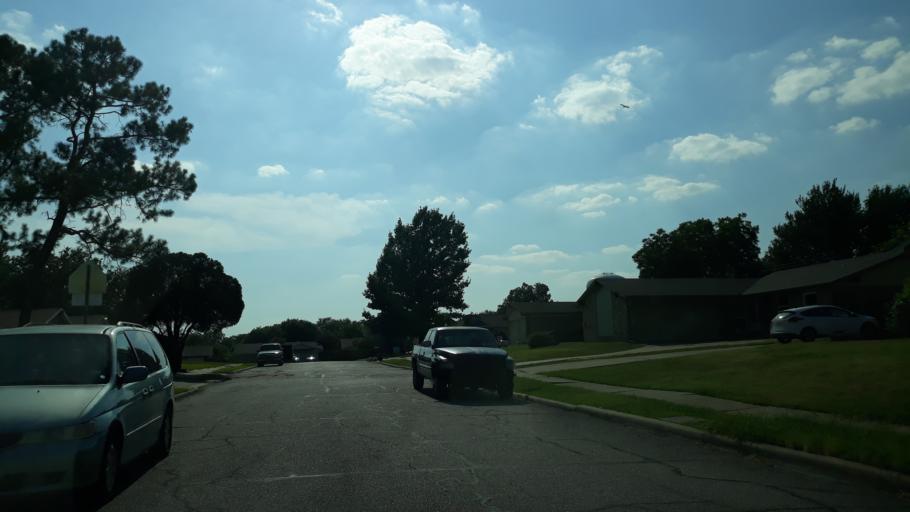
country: US
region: Texas
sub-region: Dallas County
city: Irving
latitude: 32.8433
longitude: -97.0057
